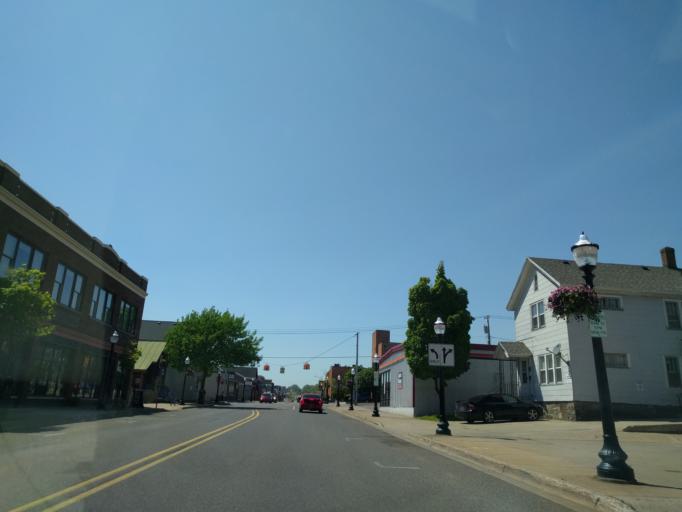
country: US
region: Michigan
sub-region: Marquette County
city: Marquette
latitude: 46.5442
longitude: -87.3988
